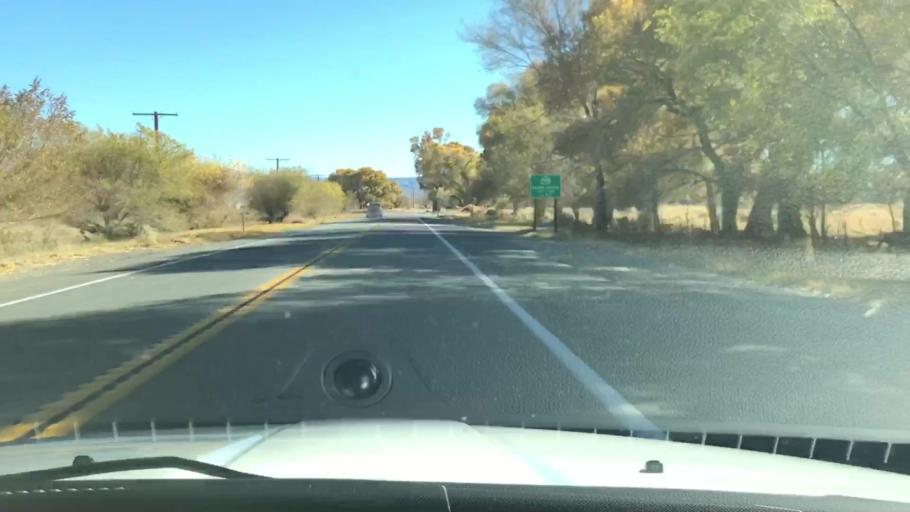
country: US
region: California
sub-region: Inyo County
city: Lone Pine
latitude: 36.2852
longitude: -118.0090
